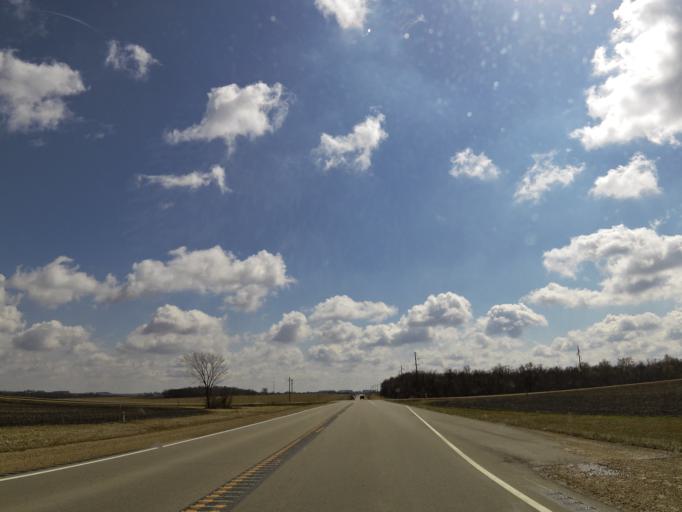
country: US
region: Minnesota
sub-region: Goodhue County
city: Kenyon
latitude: 44.2998
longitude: -92.9798
